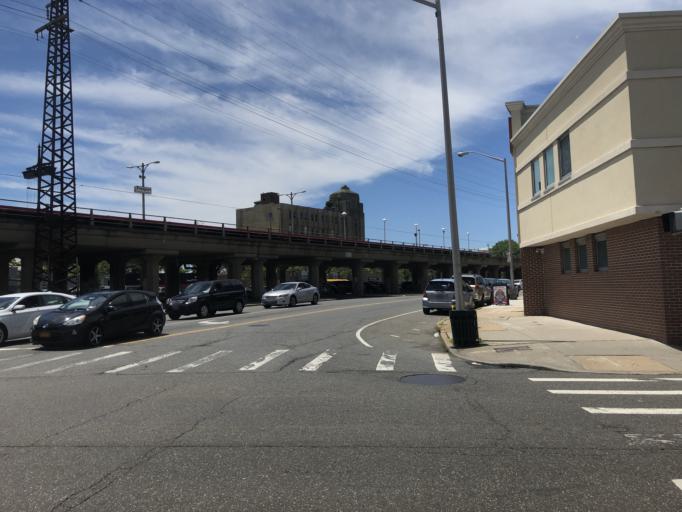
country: US
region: New York
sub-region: Nassau County
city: Freeport
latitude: 40.6576
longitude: -73.5837
